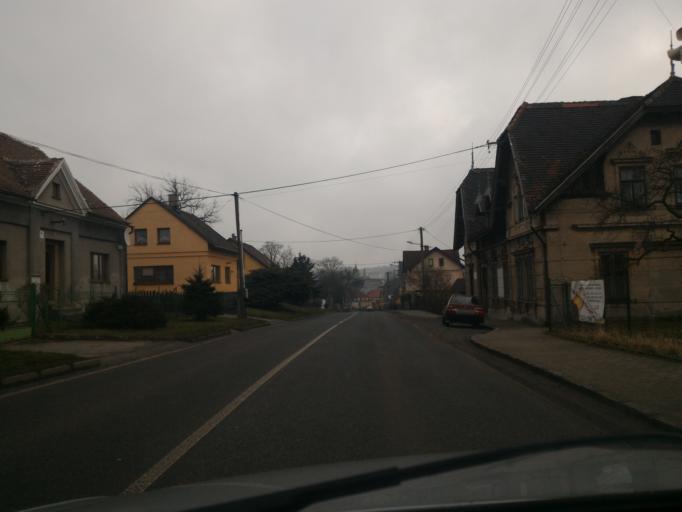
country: CZ
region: Liberecky
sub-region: Okres Liberec
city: Frydlant
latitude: 50.9197
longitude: 15.0688
